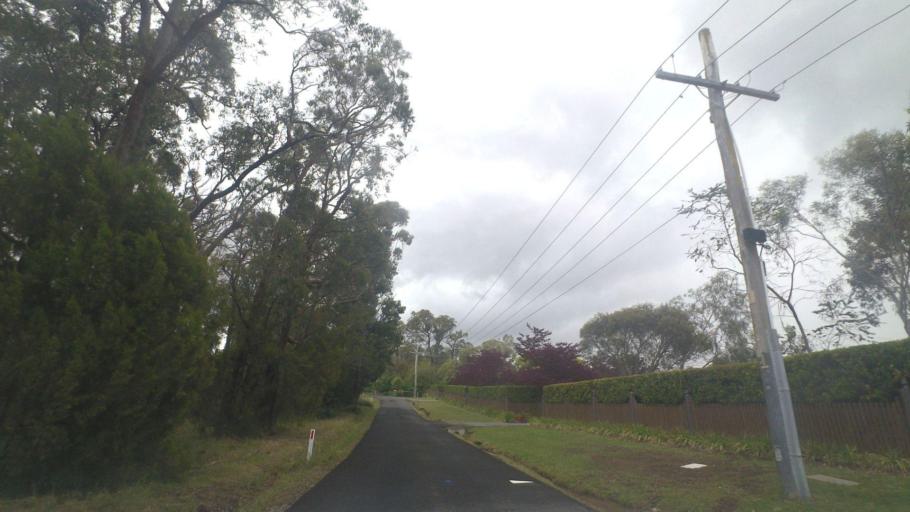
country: AU
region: Victoria
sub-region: Yarra Ranges
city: Mount Evelyn
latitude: -37.7792
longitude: 145.3719
